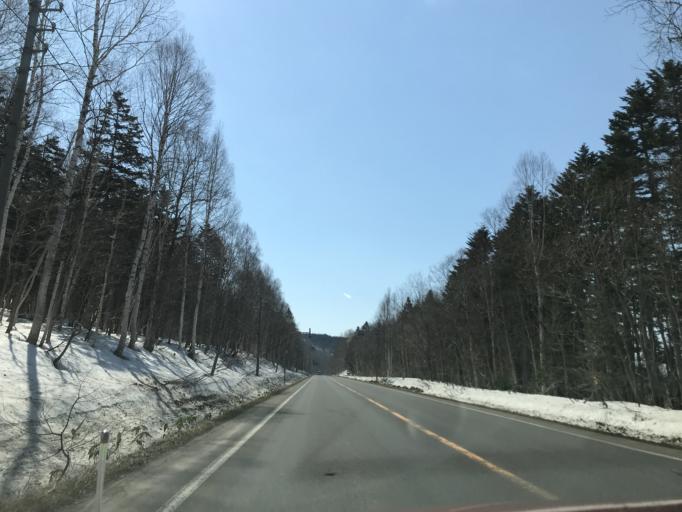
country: JP
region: Hokkaido
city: Nayoro
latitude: 44.7155
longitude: 142.2726
